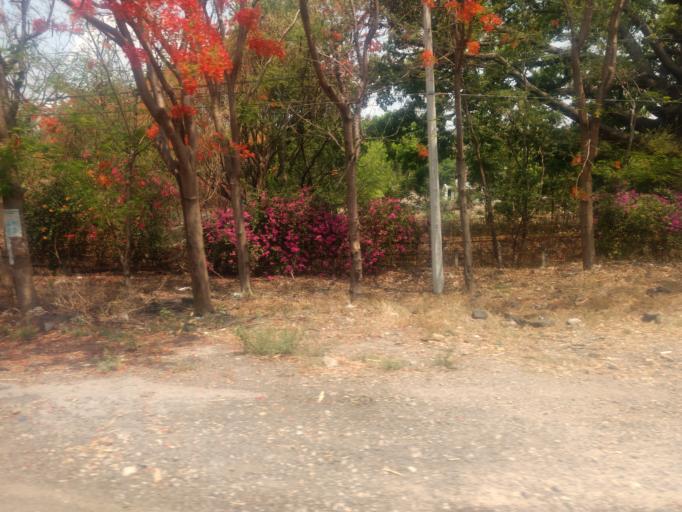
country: MX
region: Morelos
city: Puente de Ixtla
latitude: 18.6406
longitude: -99.3072
